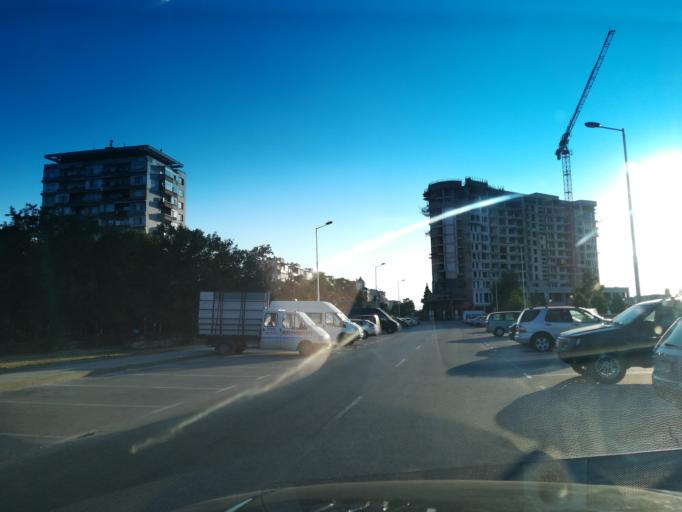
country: BG
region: Plovdiv
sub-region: Obshtina Plovdiv
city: Plovdiv
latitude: 42.1391
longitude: 24.7244
